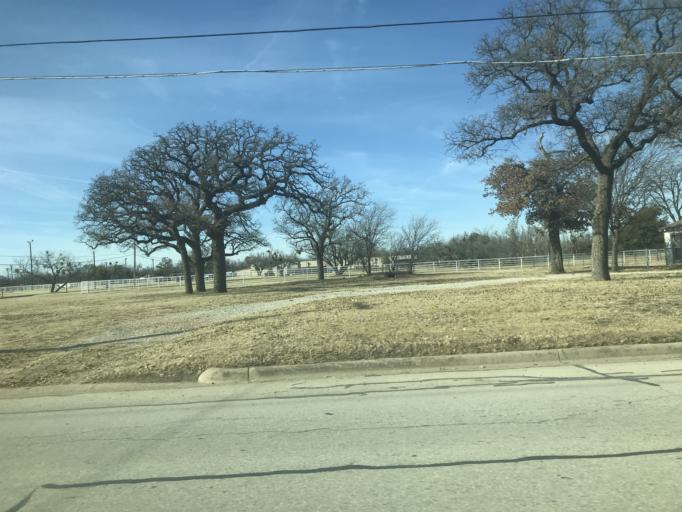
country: US
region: Texas
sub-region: Taylor County
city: Abilene
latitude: 32.4843
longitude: -99.7394
